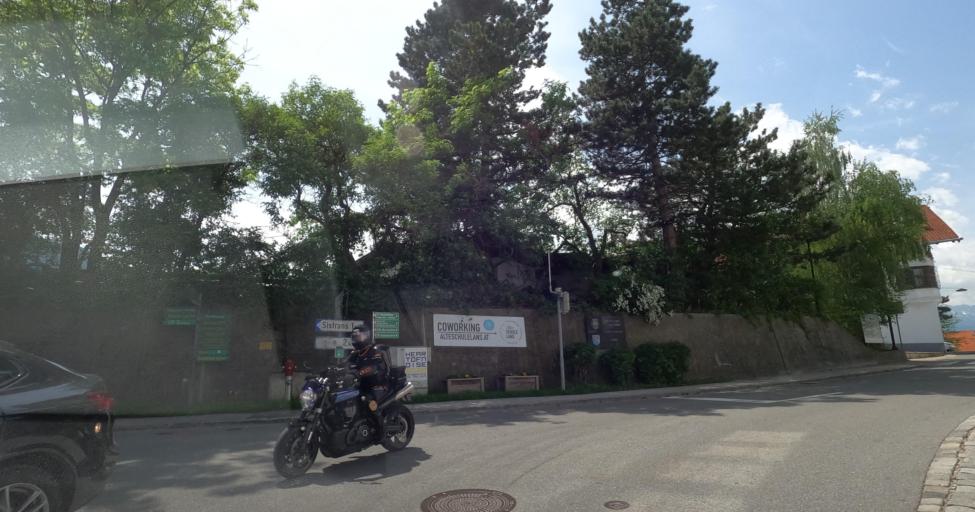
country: AT
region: Tyrol
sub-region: Politischer Bezirk Innsbruck Land
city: Sistrans
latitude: 47.2385
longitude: 11.4337
